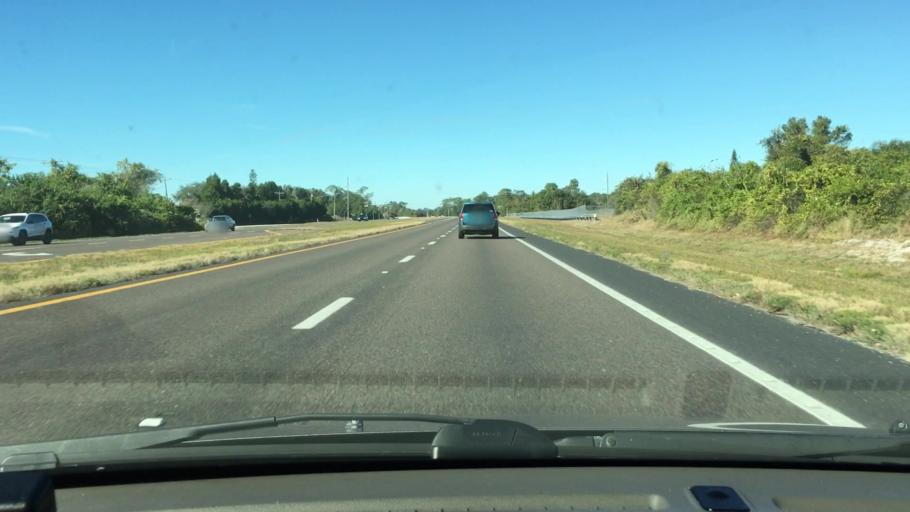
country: US
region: Florida
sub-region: Osceola County
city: Saint Cloud
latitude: 28.2370
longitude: -81.1930
